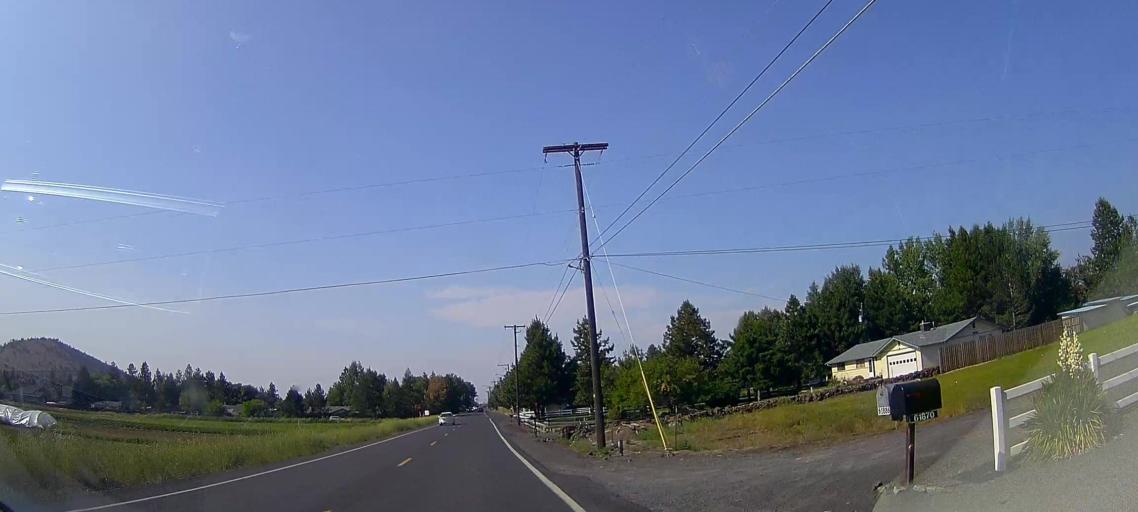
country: US
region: Oregon
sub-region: Deschutes County
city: Bend
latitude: 44.0473
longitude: -121.2686
